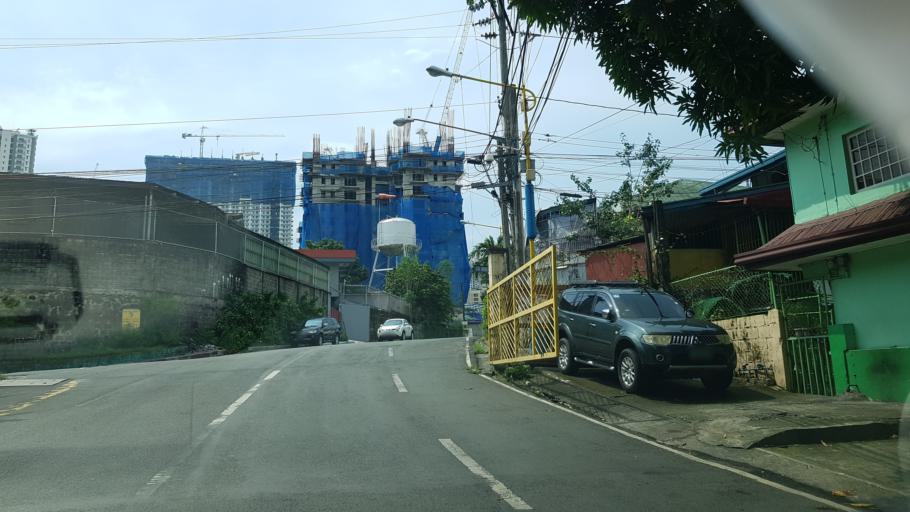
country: PH
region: Metro Manila
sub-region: Pasig
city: Pasig City
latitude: 14.5679
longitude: 121.0563
